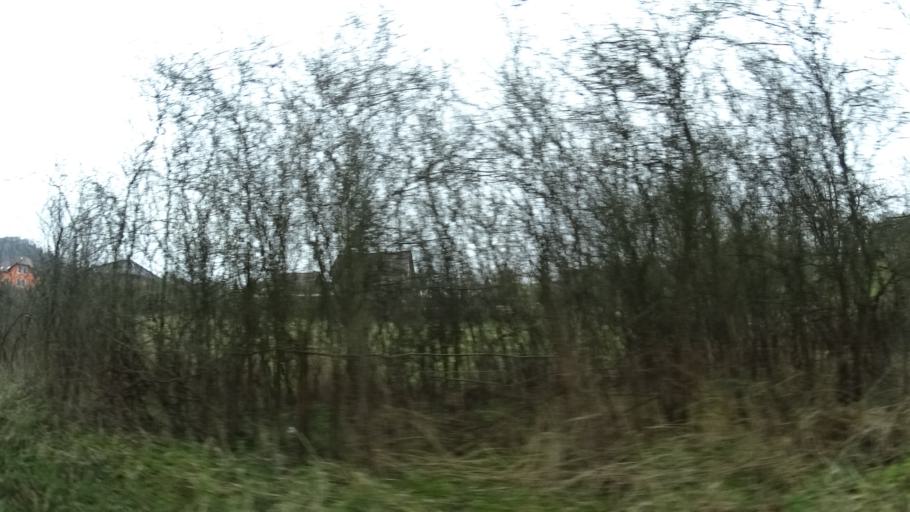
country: DE
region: Thuringia
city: Bad Blankenburg
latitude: 50.6896
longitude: 11.2517
